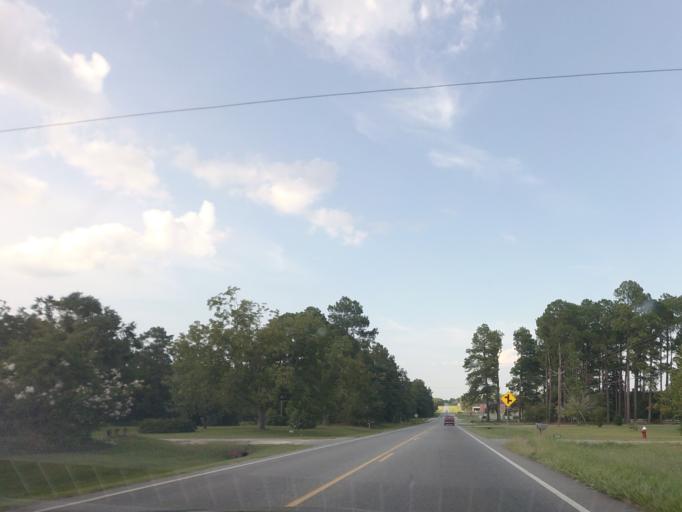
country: US
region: Georgia
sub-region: Bleckley County
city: Cochran
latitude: 32.4094
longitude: -83.3255
